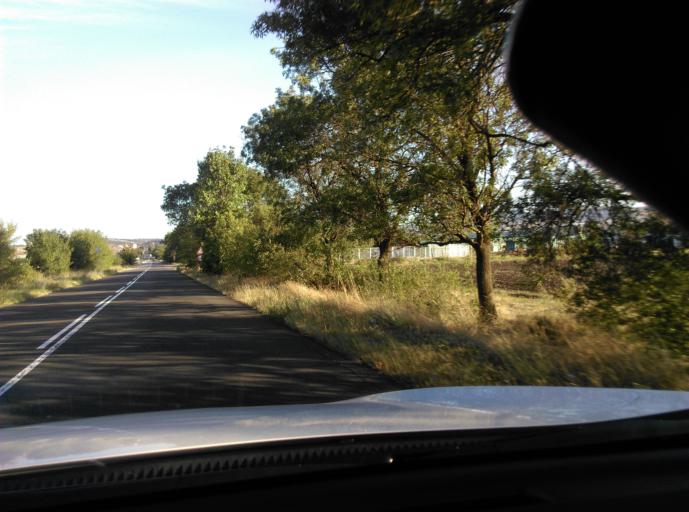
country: BG
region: Burgas
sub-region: Obshtina Kameno
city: Kameno
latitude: 42.5945
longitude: 27.3935
